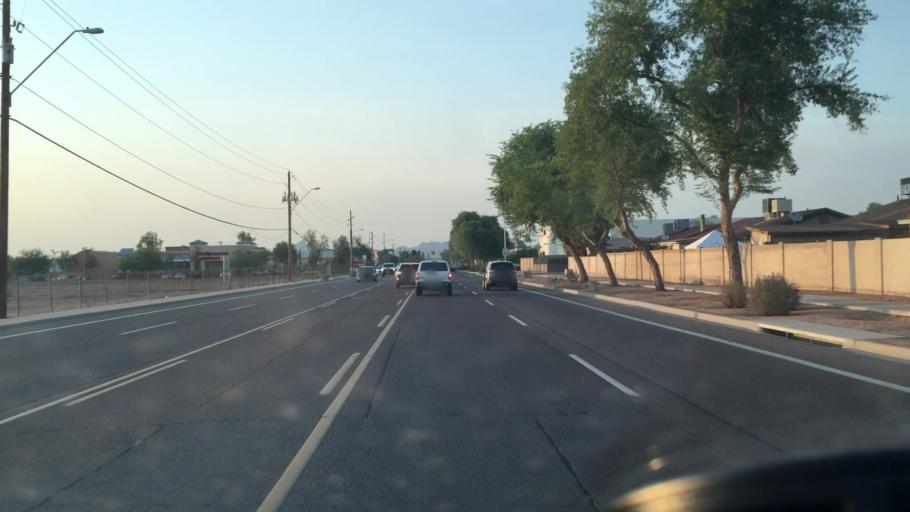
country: US
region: Arizona
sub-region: Maricopa County
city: Guadalupe
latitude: 33.3898
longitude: -111.9955
